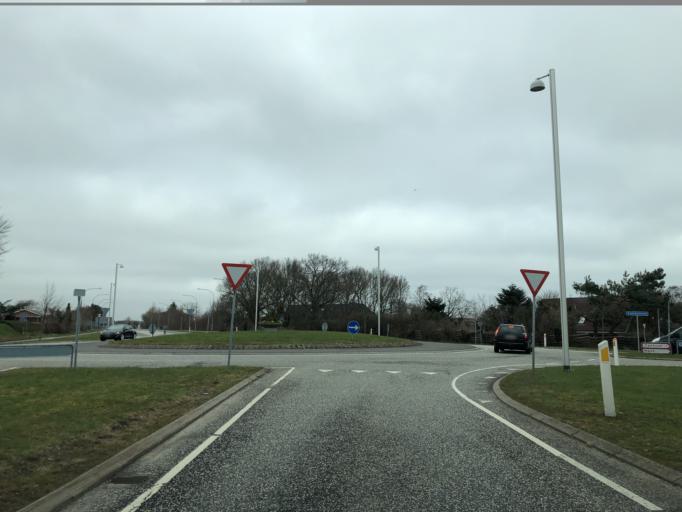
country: DK
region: North Denmark
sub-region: Frederikshavn Kommune
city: Saeby
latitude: 57.3417
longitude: 10.5152
